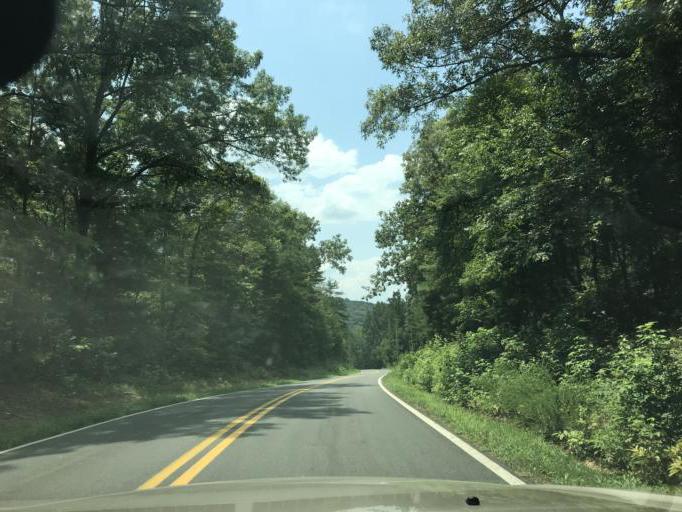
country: US
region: Georgia
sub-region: Forsyth County
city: Cumming
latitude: 34.3165
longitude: -84.2205
